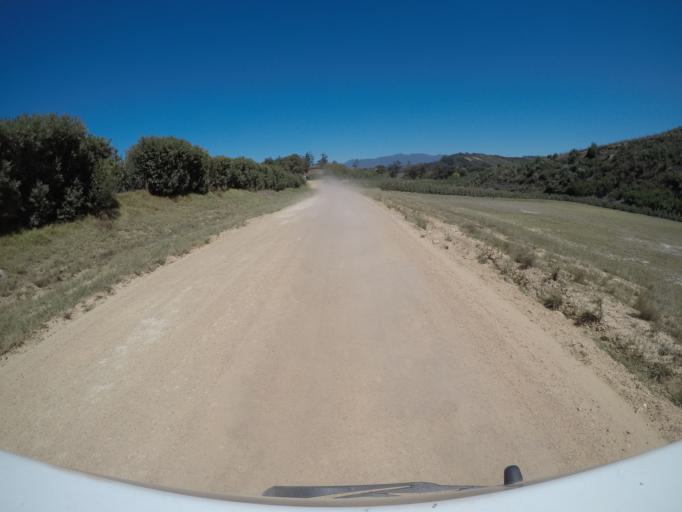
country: ZA
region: Western Cape
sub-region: Overberg District Municipality
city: Grabouw
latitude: -34.2451
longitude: 19.1025
